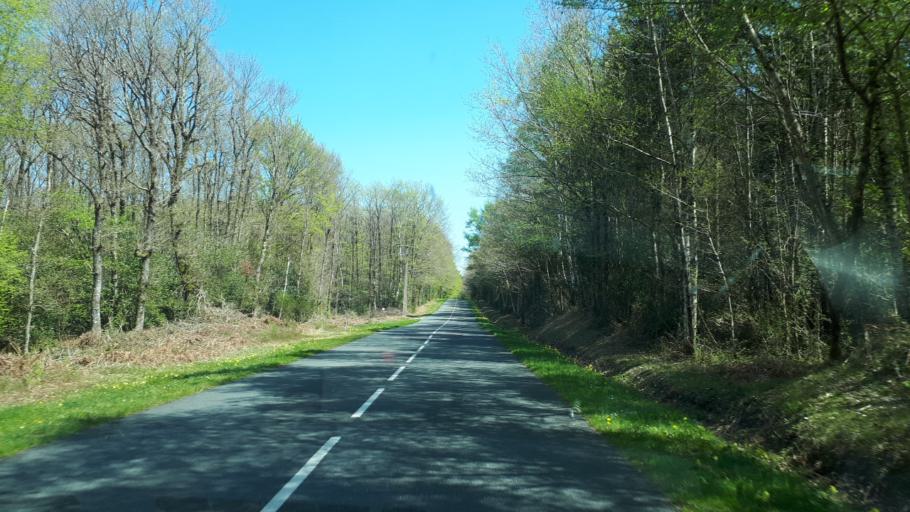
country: FR
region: Centre
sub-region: Departement du Cher
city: Henrichemont
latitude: 47.2921
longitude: 2.6020
